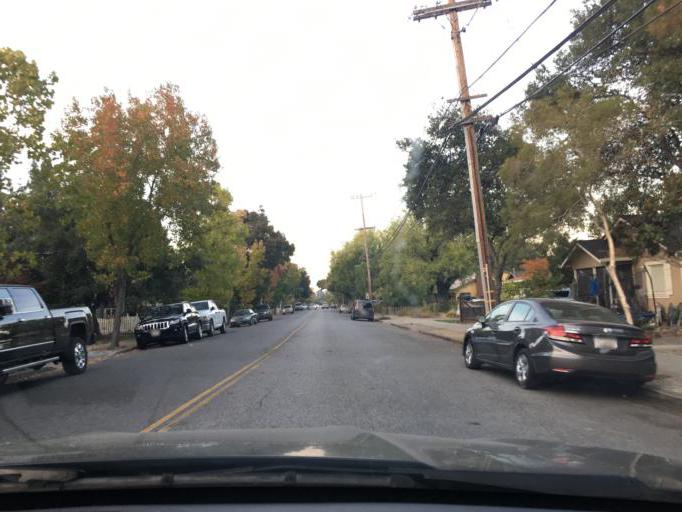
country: US
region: California
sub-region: Santa Clara County
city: Los Gatos
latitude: 37.2288
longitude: -121.9793
